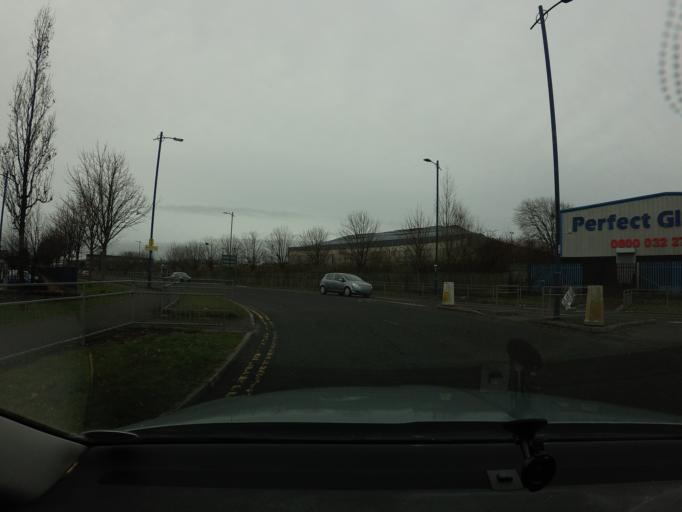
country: GB
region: Scotland
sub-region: Glasgow City
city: Glasgow
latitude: 55.8407
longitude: -4.2436
